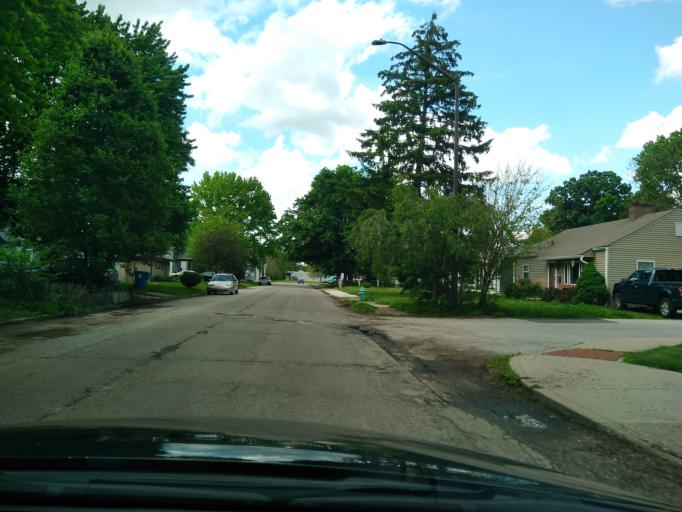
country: US
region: Indiana
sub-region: Marion County
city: Broad Ripple
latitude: 39.8461
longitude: -86.1266
